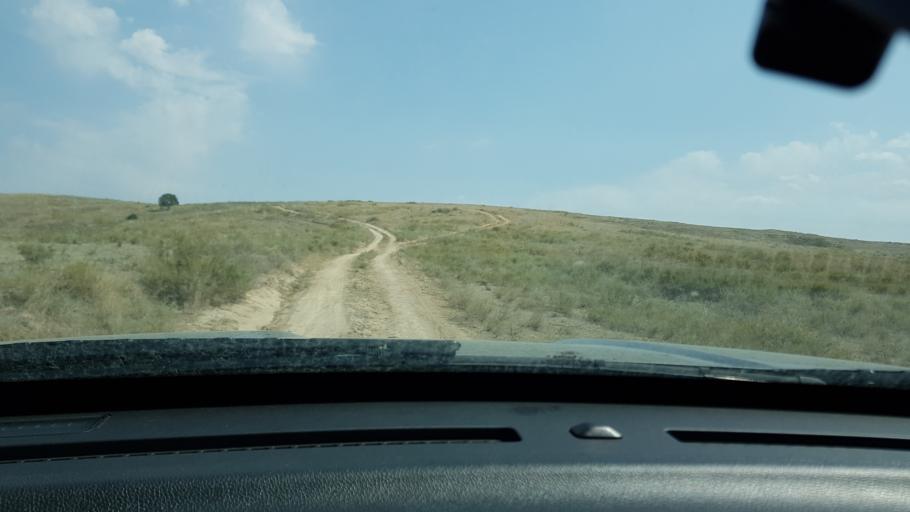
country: TM
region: Ahal
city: Baharly
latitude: 38.4095
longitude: 56.9167
